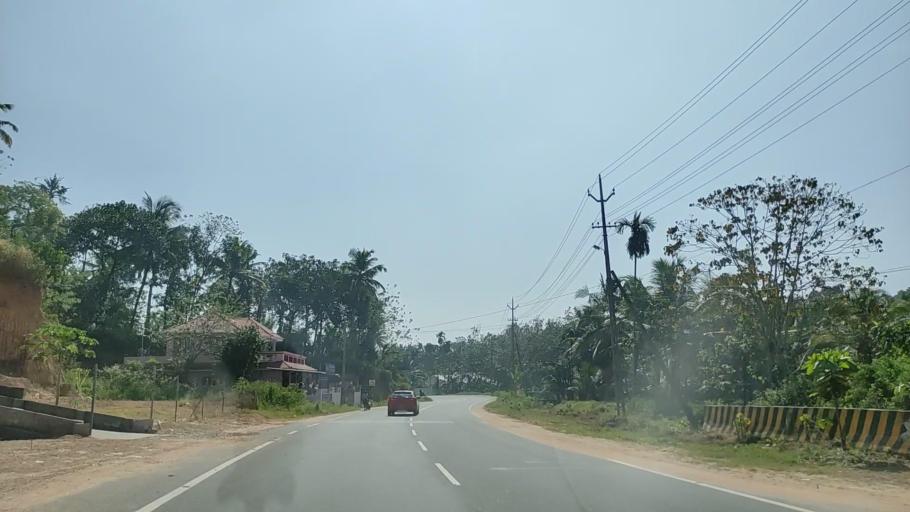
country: IN
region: Kerala
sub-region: Kollam
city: Punalur
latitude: 8.9108
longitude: 77.0484
